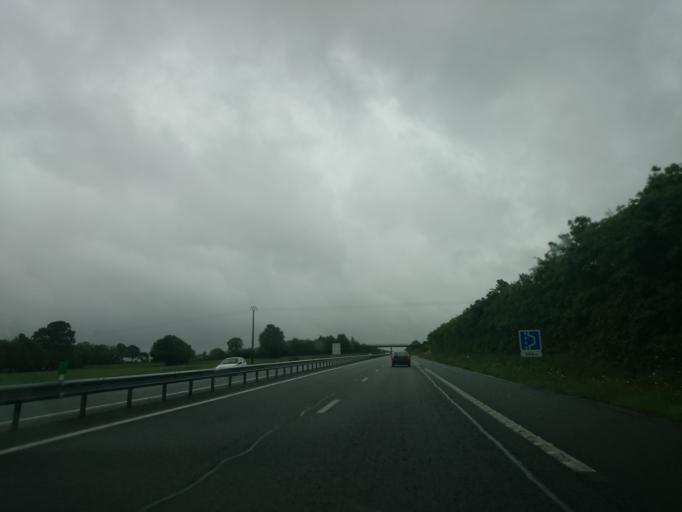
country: FR
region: Brittany
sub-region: Departement d'Ille-et-Vilaine
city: Plelan-le-Grand
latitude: 47.9918
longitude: -2.0980
